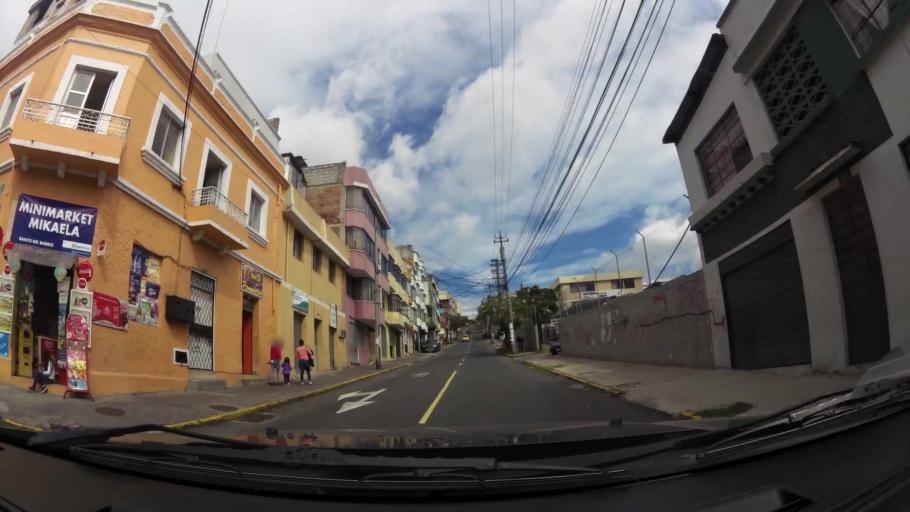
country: EC
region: Pichincha
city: Quito
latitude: -0.2150
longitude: -78.4970
